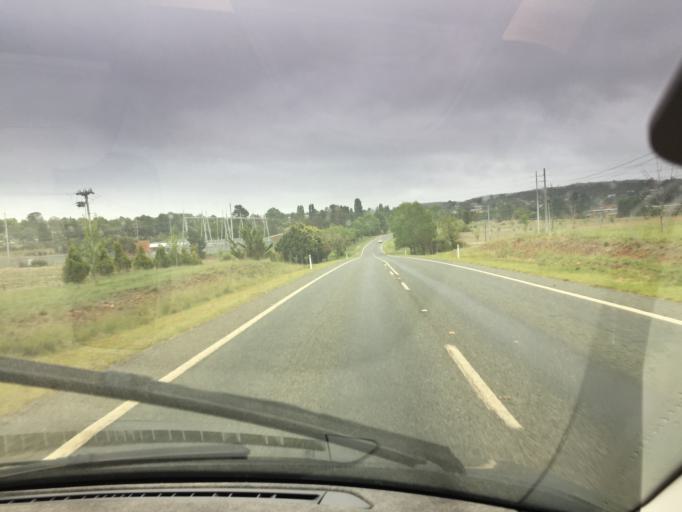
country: AU
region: New South Wales
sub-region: Cooma-Monaro
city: Cooma
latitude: -36.2164
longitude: 149.1430
